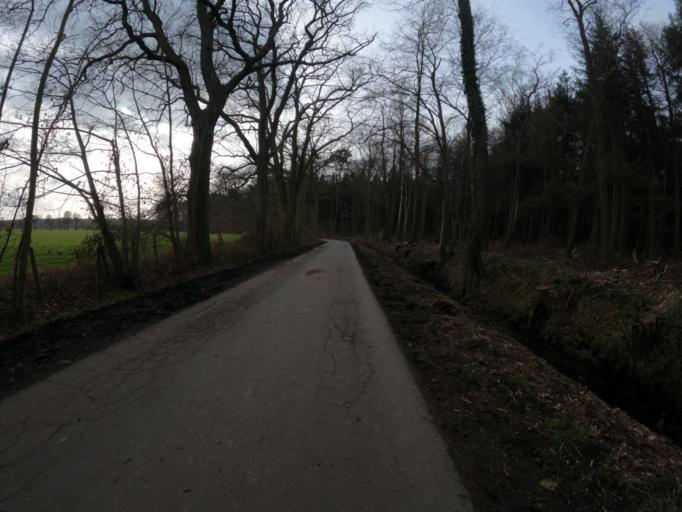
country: DE
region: Schleswig-Holstein
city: Rellingen
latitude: 53.6067
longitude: 9.7846
